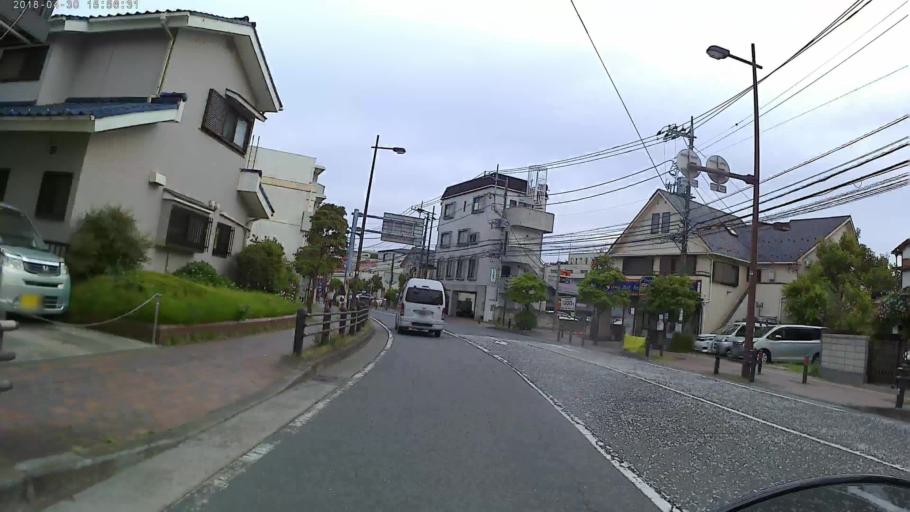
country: JP
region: Tokyo
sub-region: Machida-shi
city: Machida
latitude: 35.5318
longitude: 139.4308
